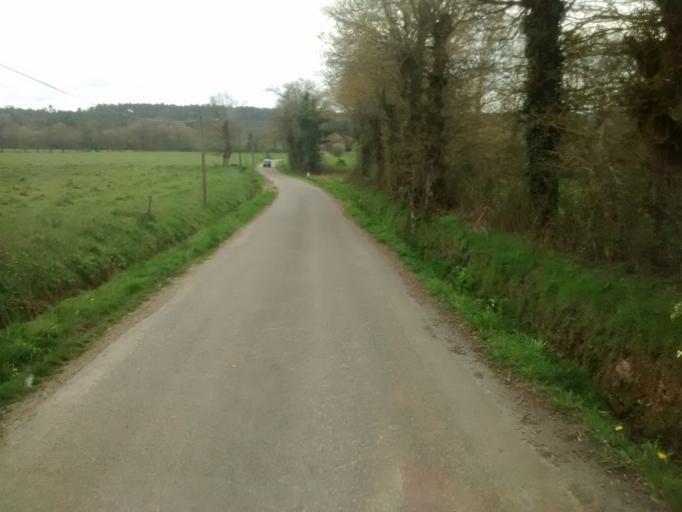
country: FR
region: Brittany
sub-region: Departement du Morbihan
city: Caro
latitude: 47.8782
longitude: -2.3600
